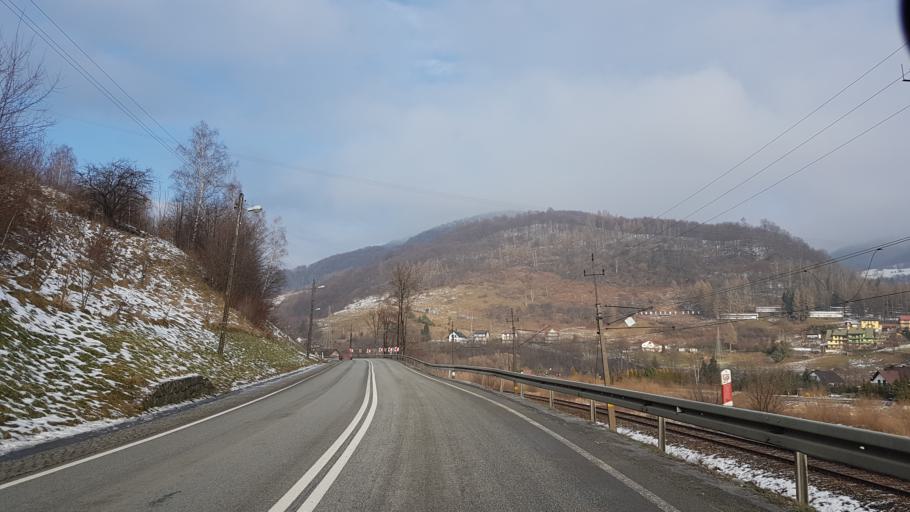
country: PL
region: Lesser Poland Voivodeship
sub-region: Powiat nowosadecki
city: Piwniczna-Zdroj
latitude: 49.4660
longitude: 20.6977
